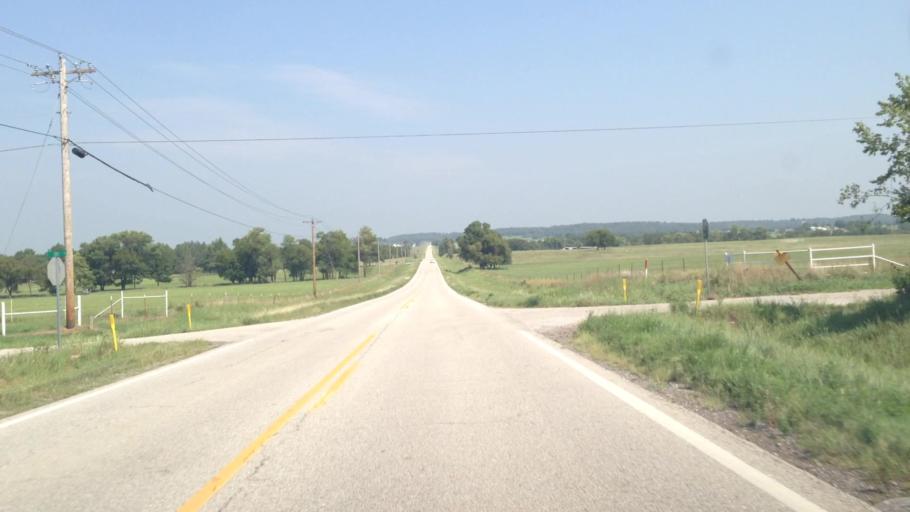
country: US
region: Oklahoma
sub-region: Craig County
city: Vinita
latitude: 36.7427
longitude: -95.1438
